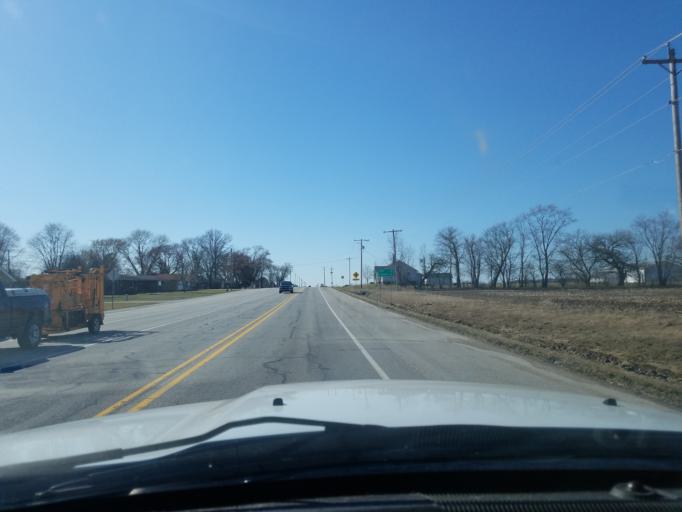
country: US
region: Indiana
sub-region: Shelby County
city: Shelbyville
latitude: 39.5046
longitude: -85.8023
